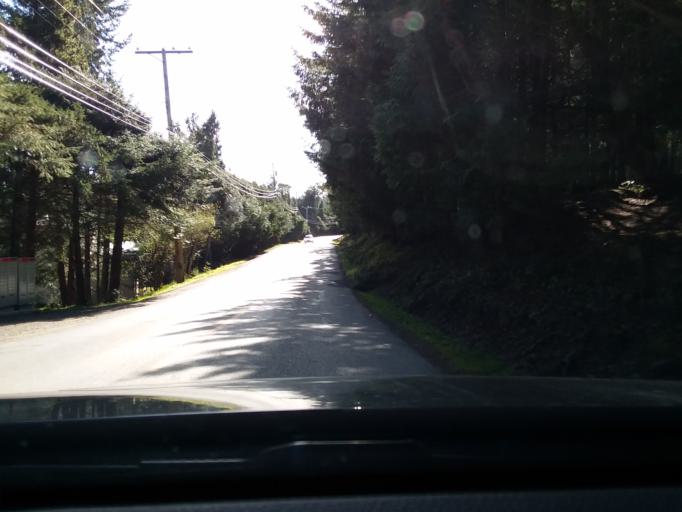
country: CA
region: British Columbia
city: North Saanich
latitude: 48.8836
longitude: -123.3300
